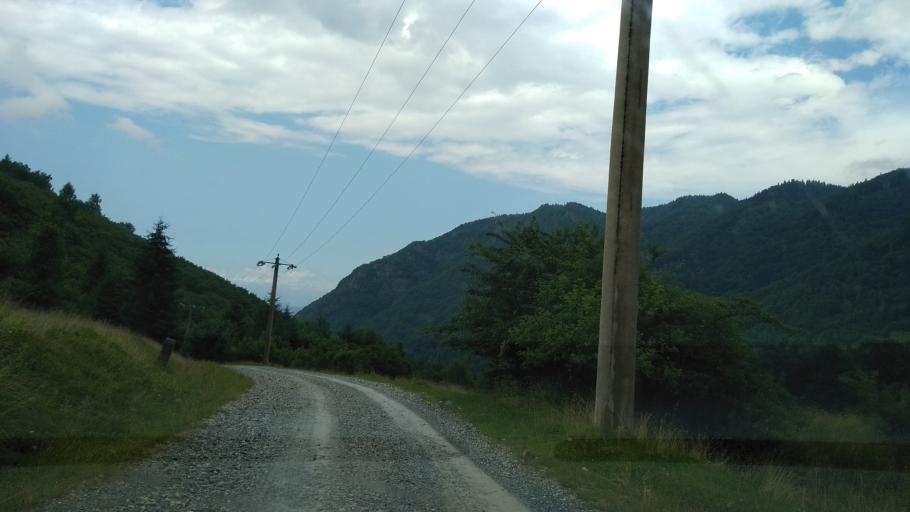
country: RO
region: Hunedoara
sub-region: Comuna Rau de Mori
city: Rau de Mori
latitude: 45.4481
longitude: 22.8952
